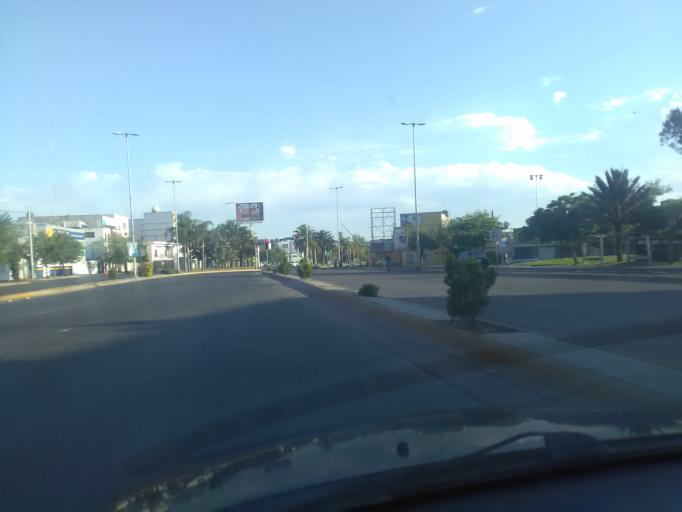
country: MX
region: Durango
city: Victoria de Durango
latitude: 24.0193
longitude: -104.6643
